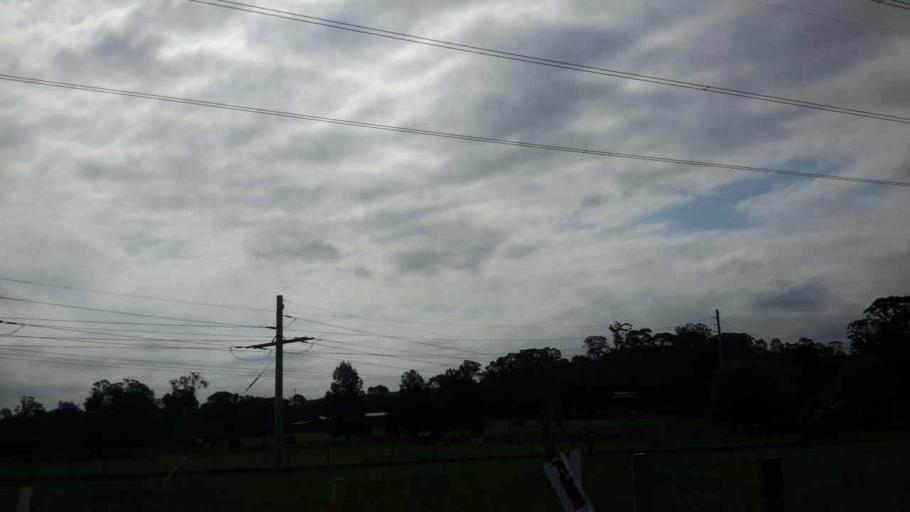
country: AU
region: New South Wales
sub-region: Campbelltown Municipality
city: Glen Alpine
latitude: -34.0939
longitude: 150.7699
